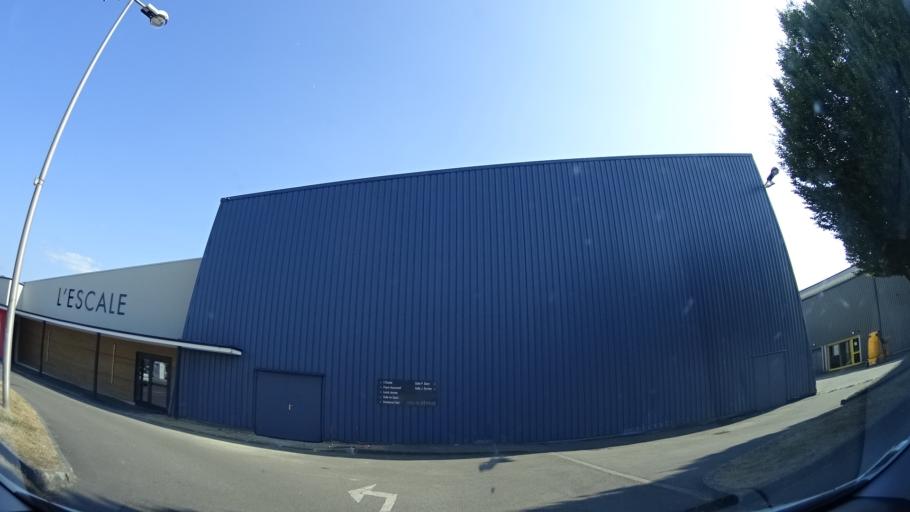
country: FR
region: Brittany
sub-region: Departement d'Ille-et-Vilaine
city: Geveze
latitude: 48.2211
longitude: -1.7936
